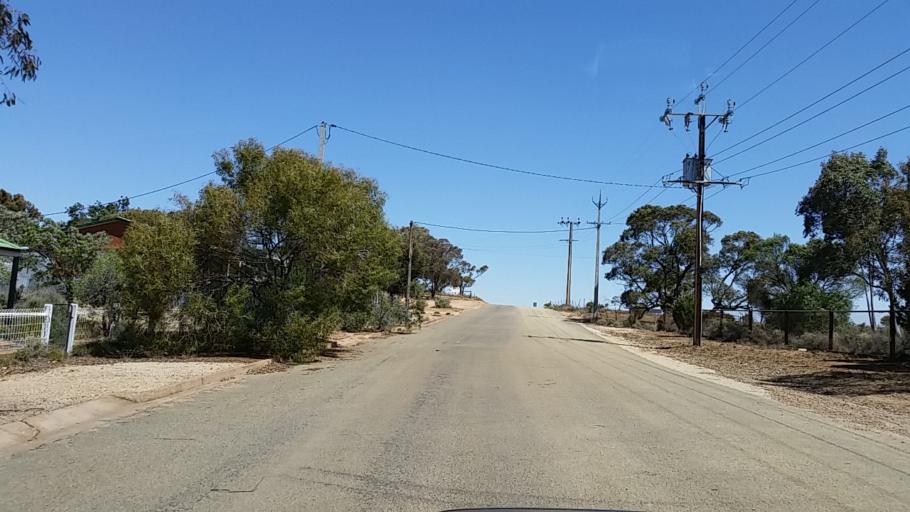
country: AU
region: South Australia
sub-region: Peterborough
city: Peterborough
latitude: -32.9812
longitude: 138.8318
